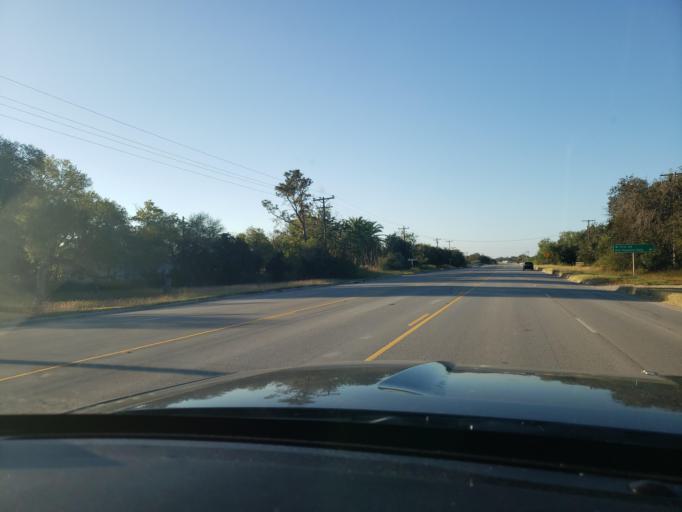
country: US
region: Texas
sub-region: Bee County
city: Beeville
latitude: 28.4300
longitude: -97.7151
